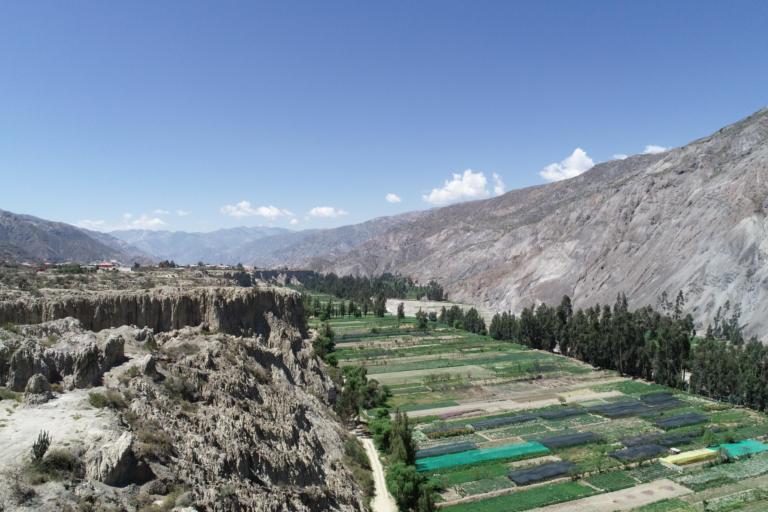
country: BO
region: La Paz
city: La Paz
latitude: -16.6363
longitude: -68.0530
